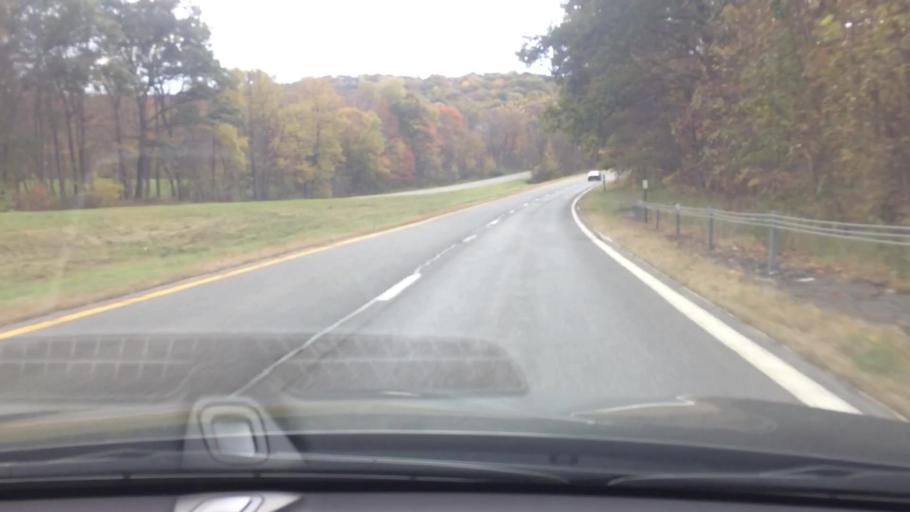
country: US
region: New York
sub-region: Dutchess County
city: Pine Plains
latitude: 41.9508
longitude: -73.7528
